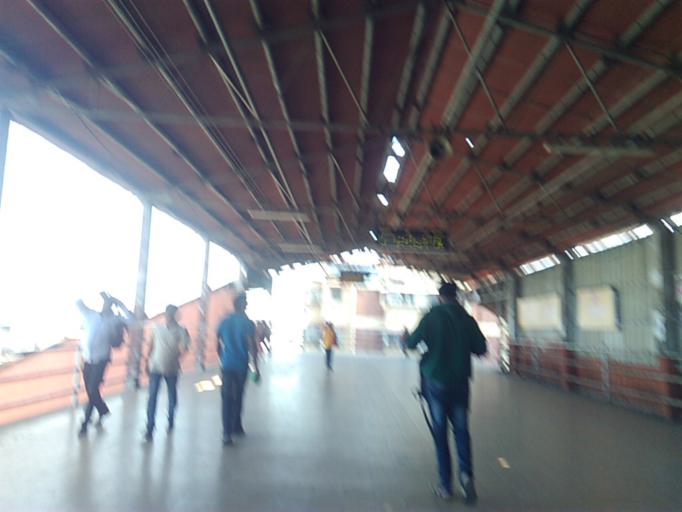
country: IN
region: Maharashtra
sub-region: Thane
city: Bhayandar
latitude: 19.3108
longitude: 72.8527
